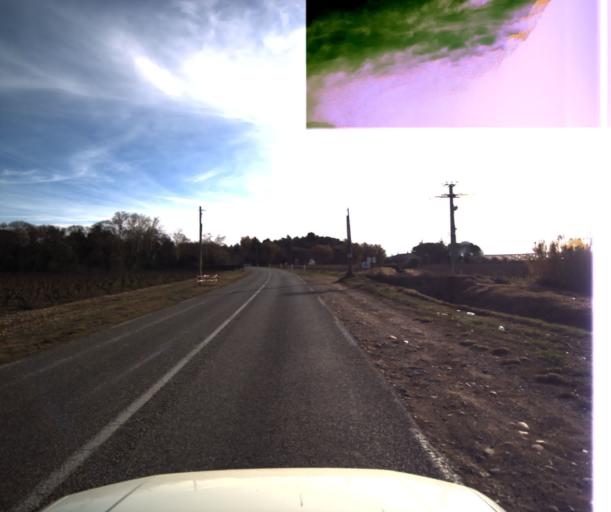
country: FR
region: Provence-Alpes-Cote d'Azur
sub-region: Departement du Vaucluse
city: Villelaure
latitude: 43.7016
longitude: 5.4523
